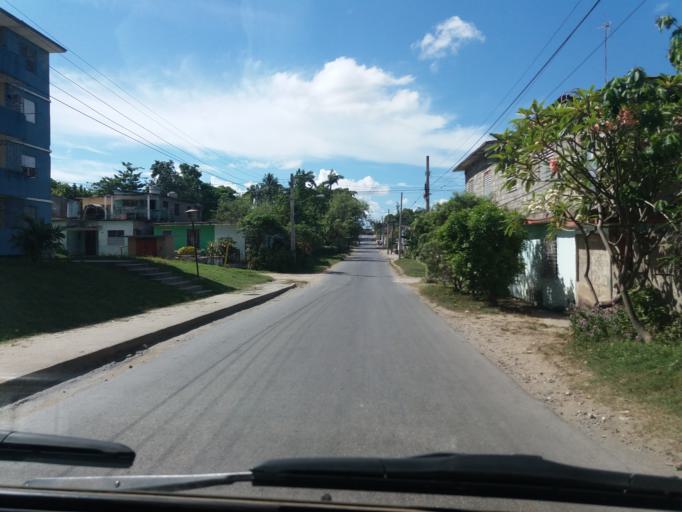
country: CU
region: Cienfuegos
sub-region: Municipio de Cienfuegos
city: Cienfuegos
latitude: 22.1496
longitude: -80.4271
